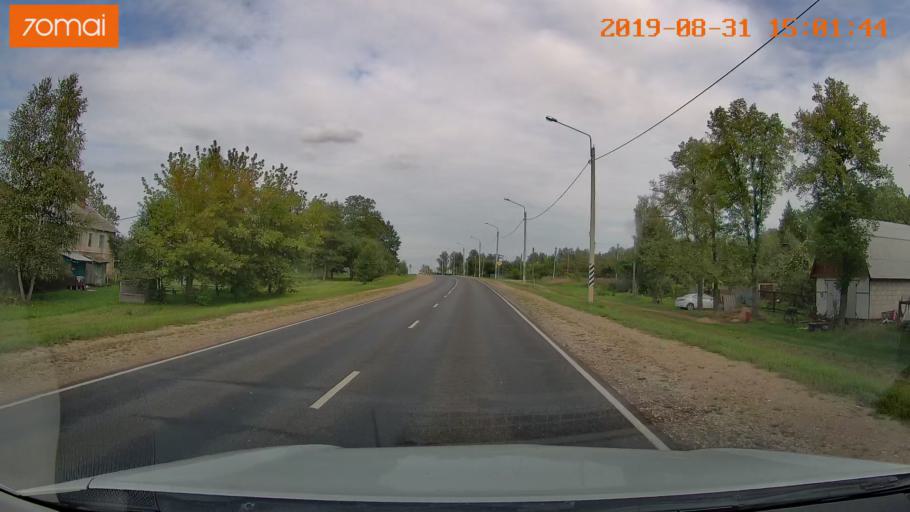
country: RU
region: Kaluga
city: Spas-Demensk
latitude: 54.3412
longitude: 34.0629
